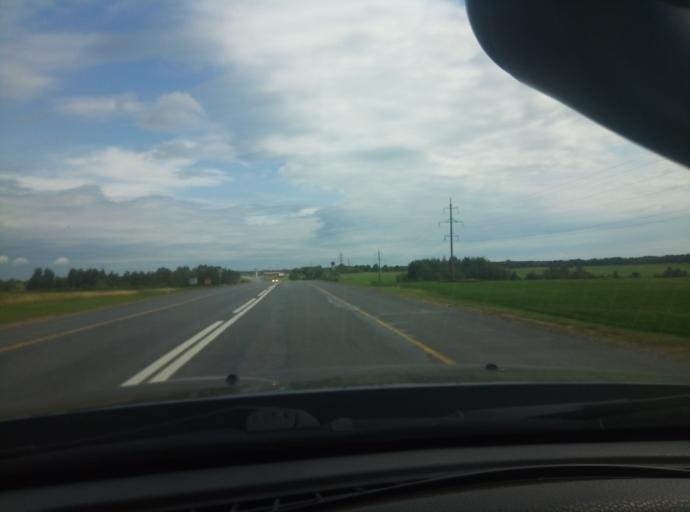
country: RU
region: Tula
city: Barsuki
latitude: 54.2484
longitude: 37.5223
